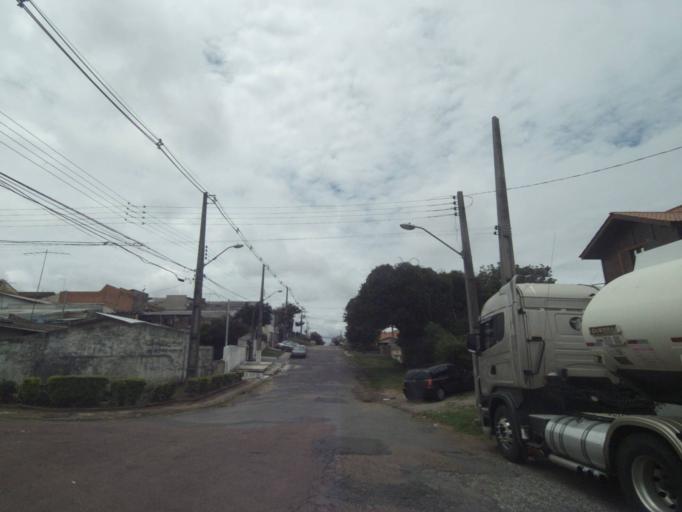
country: BR
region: Parana
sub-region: Curitiba
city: Curitiba
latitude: -25.4866
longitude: -49.2877
